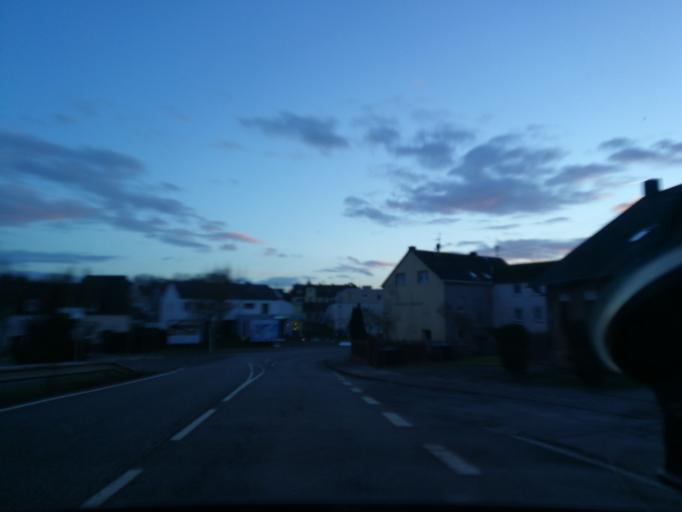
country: DE
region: Rheinland-Pfalz
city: Kenn
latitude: 49.8245
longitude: 6.7045
